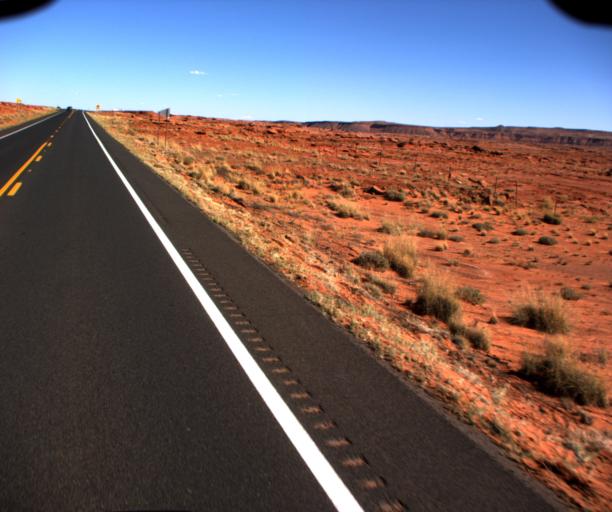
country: US
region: Arizona
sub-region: Coconino County
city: Tuba City
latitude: 36.1000
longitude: -111.3233
